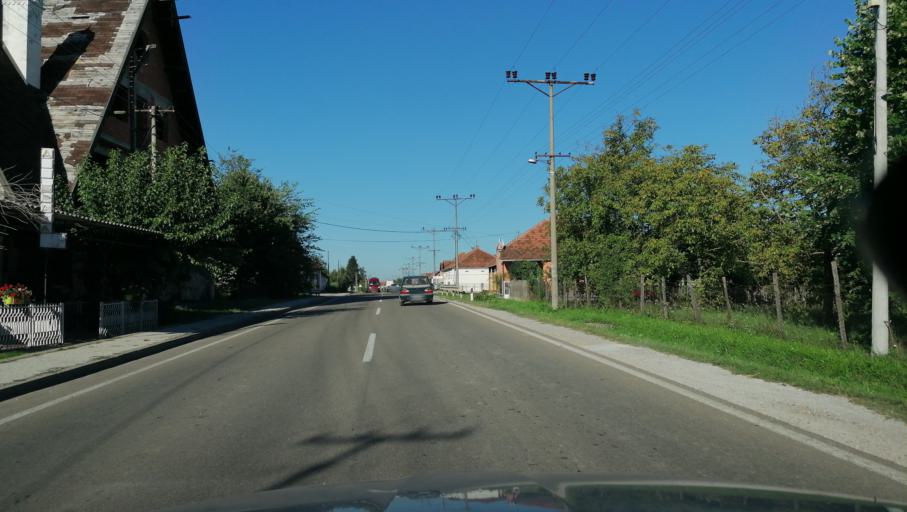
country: RS
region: Central Serbia
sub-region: Sumadijski Okrug
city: Knic
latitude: 43.9012
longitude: 20.6270
